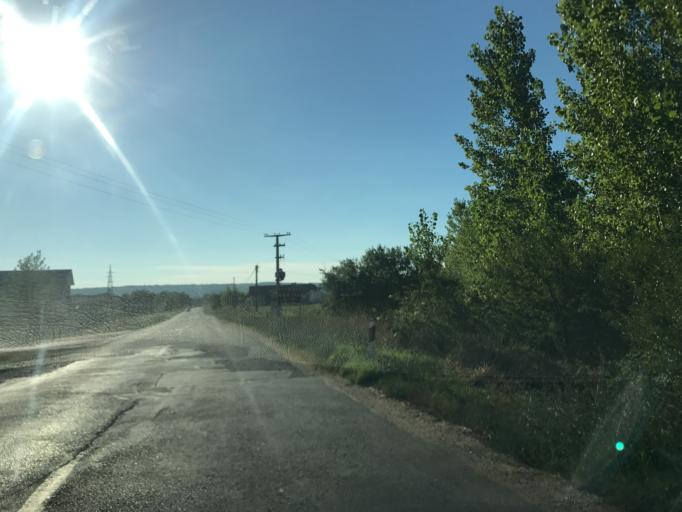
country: RS
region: Central Serbia
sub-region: Borski Okrug
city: Negotin
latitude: 44.2232
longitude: 22.5537
